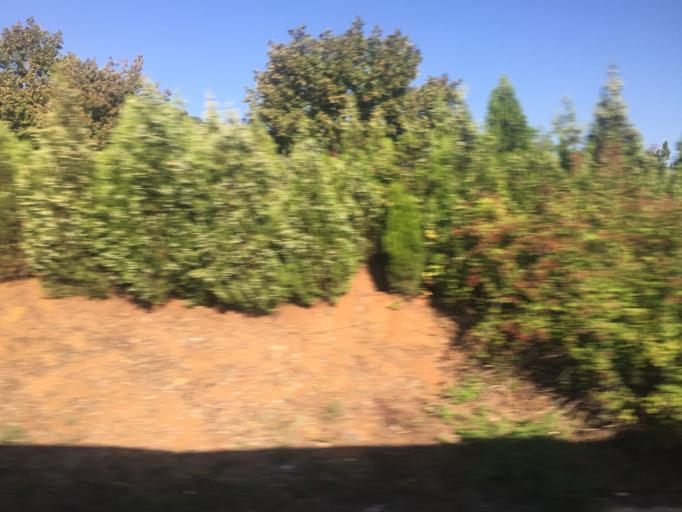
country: TR
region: Bursa
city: Yenice
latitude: 40.2000
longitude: 29.3473
